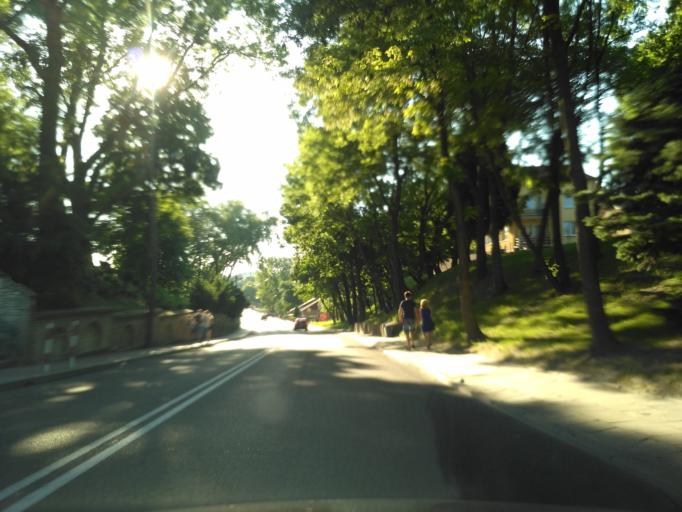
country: PL
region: Lublin Voivodeship
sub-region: Powiat lubelski
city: Bychawa
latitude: 51.0163
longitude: 22.5320
